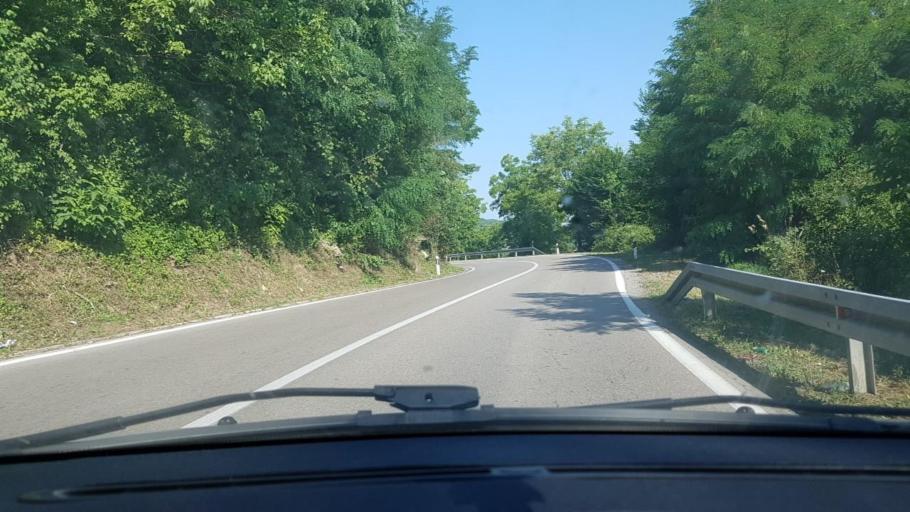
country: BA
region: Federation of Bosnia and Herzegovina
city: Pecigrad
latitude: 45.0474
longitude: 15.9070
